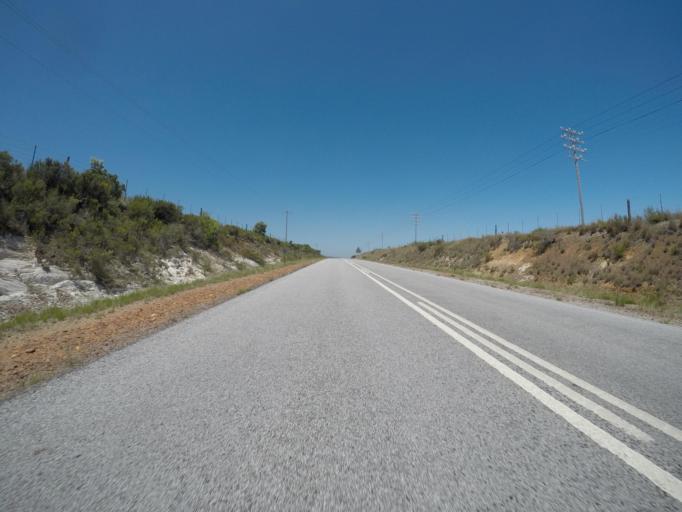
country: ZA
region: Eastern Cape
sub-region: Cacadu District Municipality
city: Kareedouw
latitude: -33.9575
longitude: 24.4002
